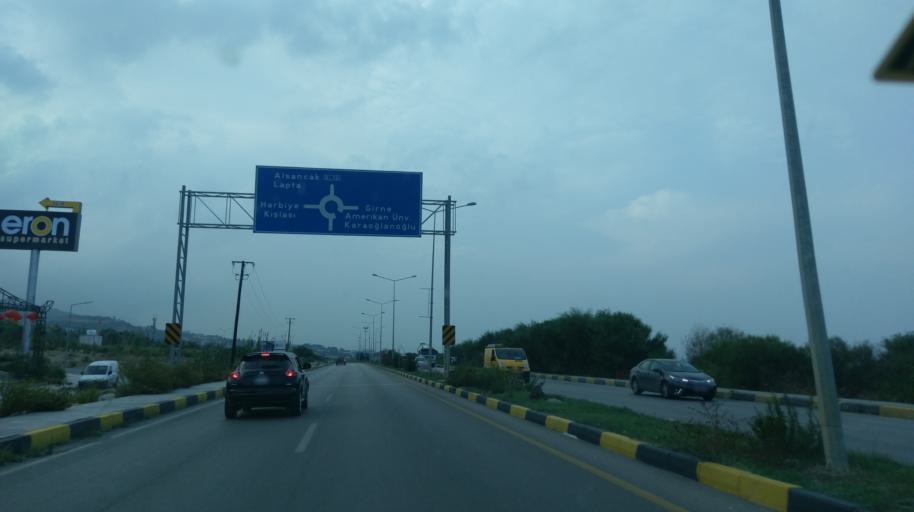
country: CY
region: Keryneia
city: Kyrenia
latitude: 35.3302
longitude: 33.2776
